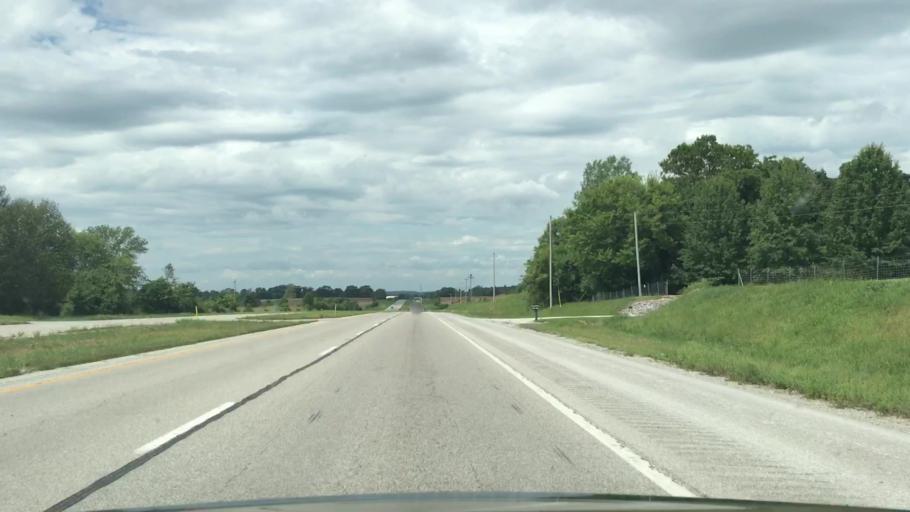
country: US
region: Kentucky
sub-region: Todd County
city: Elkton
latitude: 36.8236
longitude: -87.2030
